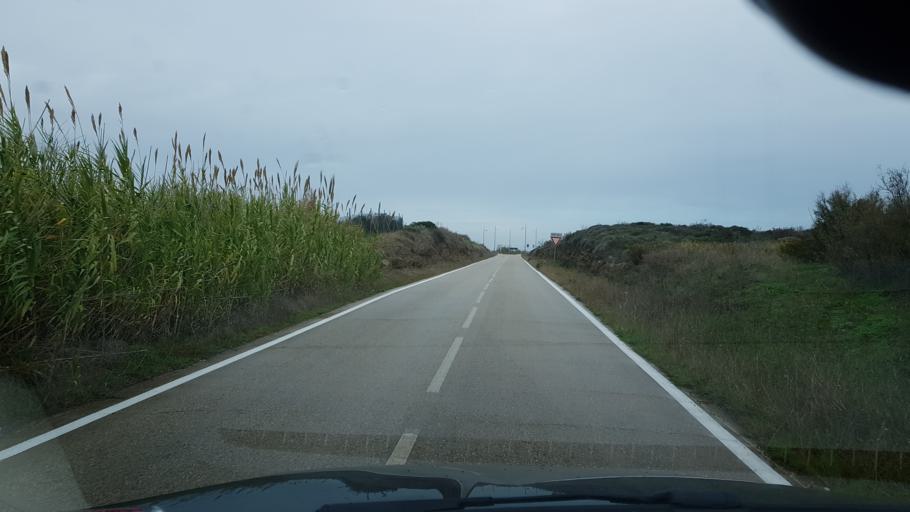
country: IT
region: Apulia
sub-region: Provincia di Brindisi
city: Brindisi
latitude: 40.6867
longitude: 17.8470
